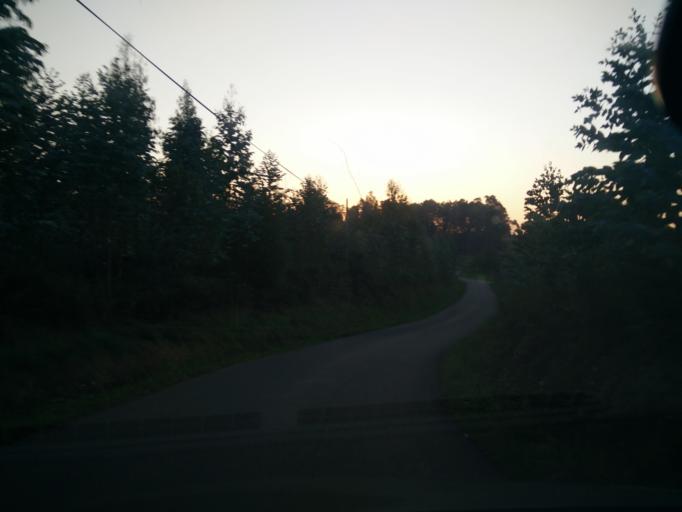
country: ES
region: Galicia
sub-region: Provincia da Coruna
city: Monfero
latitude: 43.3528
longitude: -8.0577
